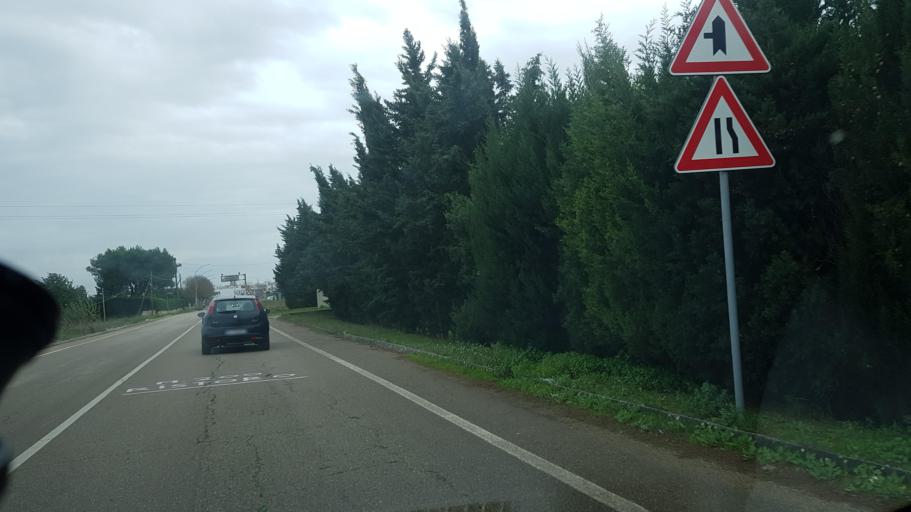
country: IT
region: Apulia
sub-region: Provincia di Lecce
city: Novoli
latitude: 40.3790
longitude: 18.0393
